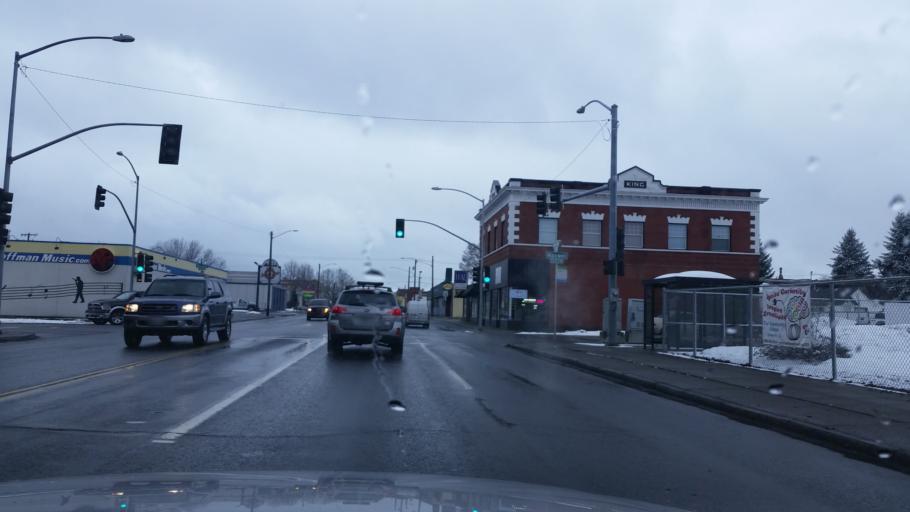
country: US
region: Washington
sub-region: Spokane County
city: Spokane
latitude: 47.6716
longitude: -117.4267
